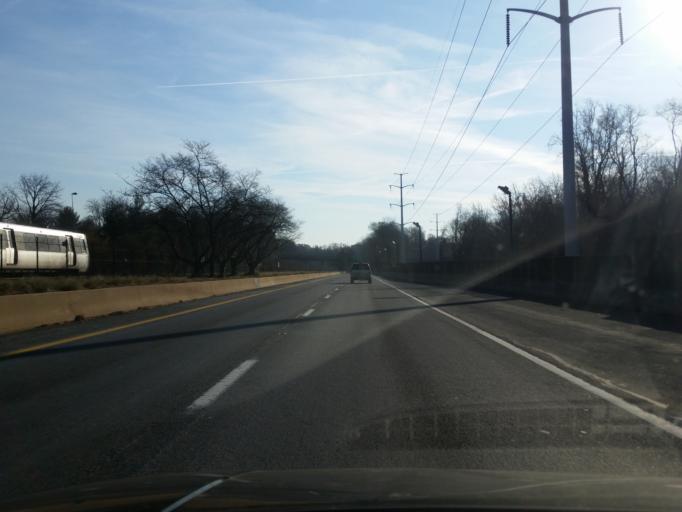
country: US
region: Virginia
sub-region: Fairfax County
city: Seven Corners
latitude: 38.8814
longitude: -77.1436
